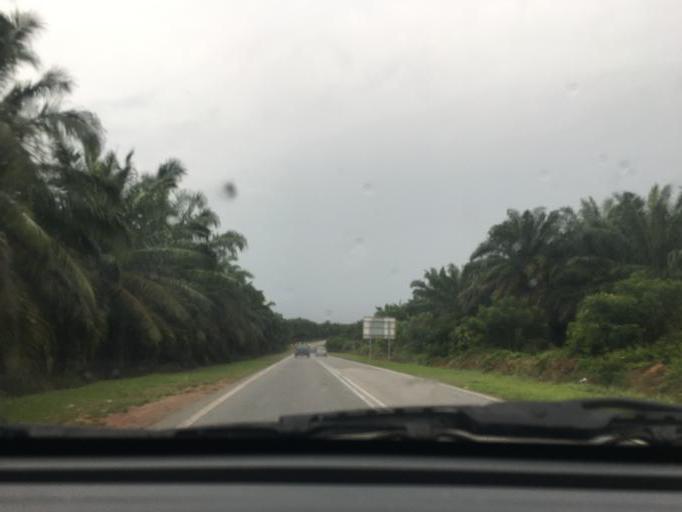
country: MY
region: Kedah
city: Sungai Petani
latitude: 5.6250
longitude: 100.6359
